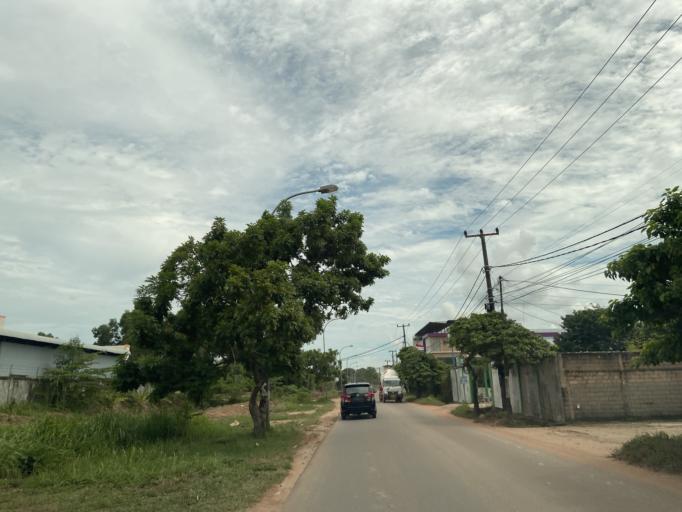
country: SG
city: Singapore
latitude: 1.0412
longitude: 103.9772
